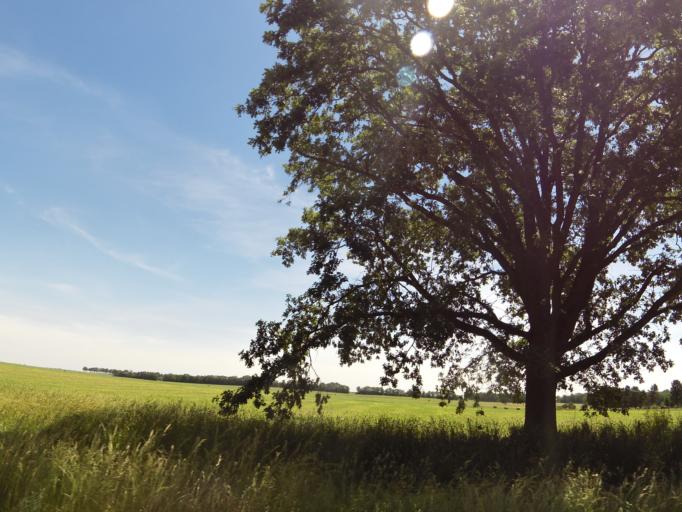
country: US
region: Illinois
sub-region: Vermilion County
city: Rossville
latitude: 40.3333
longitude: -87.6619
